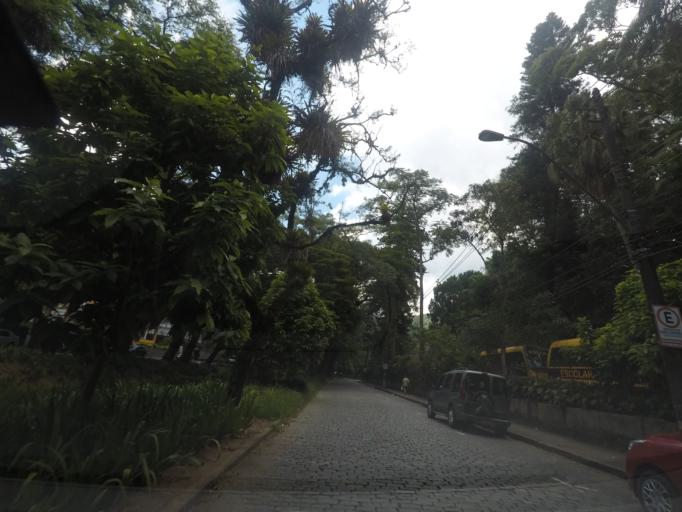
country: BR
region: Rio de Janeiro
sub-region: Petropolis
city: Petropolis
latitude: -22.5044
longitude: -43.1836
